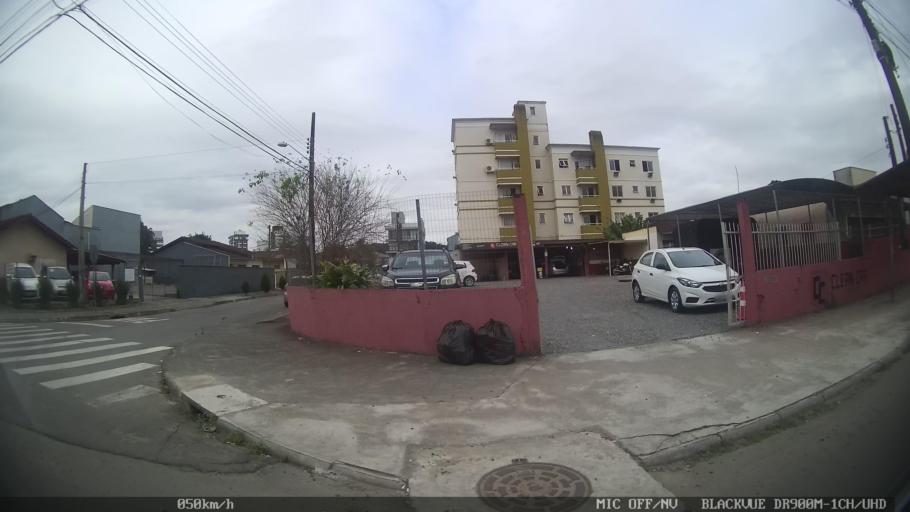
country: BR
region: Santa Catarina
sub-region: Joinville
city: Joinville
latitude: -26.2685
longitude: -48.8659
